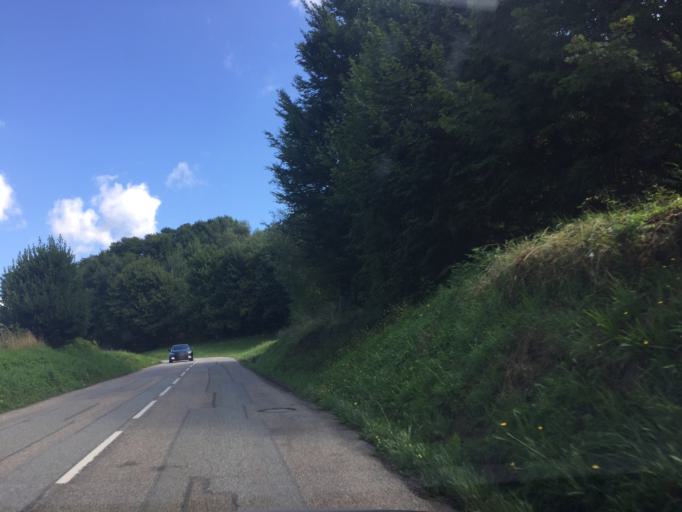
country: FR
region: Rhone-Alpes
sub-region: Departement de la Savoie
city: La Rochette
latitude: 45.4532
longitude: 6.1217
